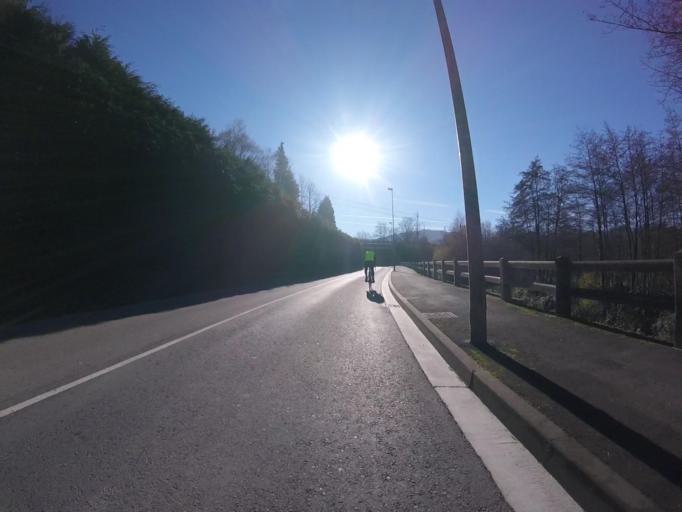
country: ES
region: Basque Country
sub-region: Provincia de Guipuzcoa
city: Irun
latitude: 43.3350
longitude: -1.7775
